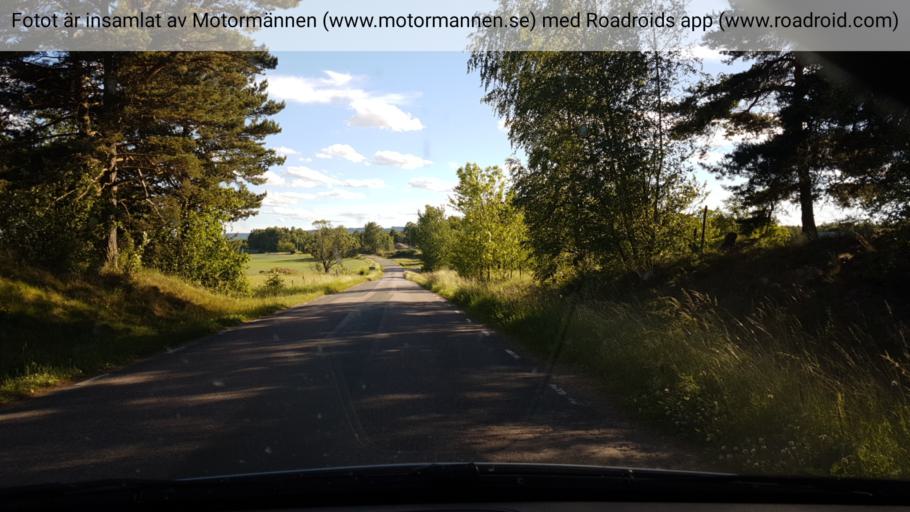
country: SE
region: Vaestra Goetaland
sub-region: Skovde Kommun
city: Stopen
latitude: 58.5357
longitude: 13.8672
